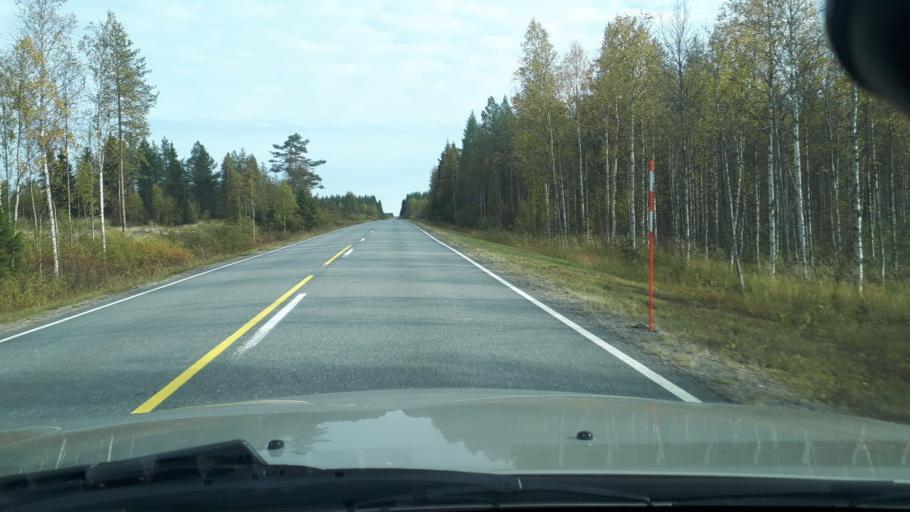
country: FI
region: Lapland
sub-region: Rovaniemi
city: Ranua
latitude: 65.9632
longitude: 26.0764
